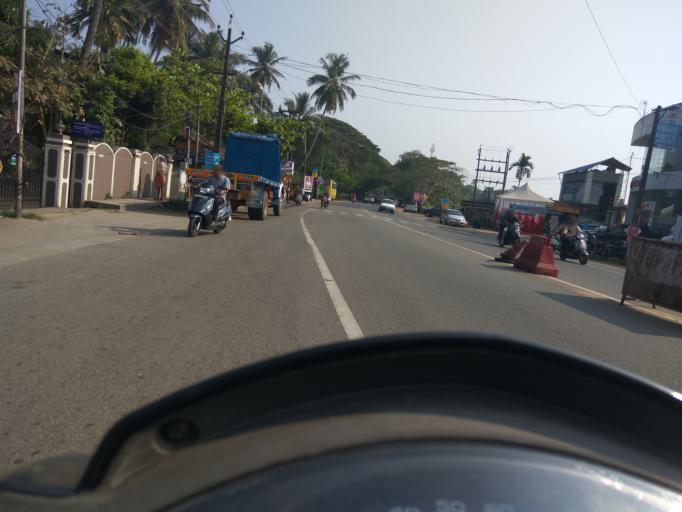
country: IN
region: Kerala
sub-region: Kozhikode
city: Kozhikode
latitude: 11.2884
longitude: 75.7668
